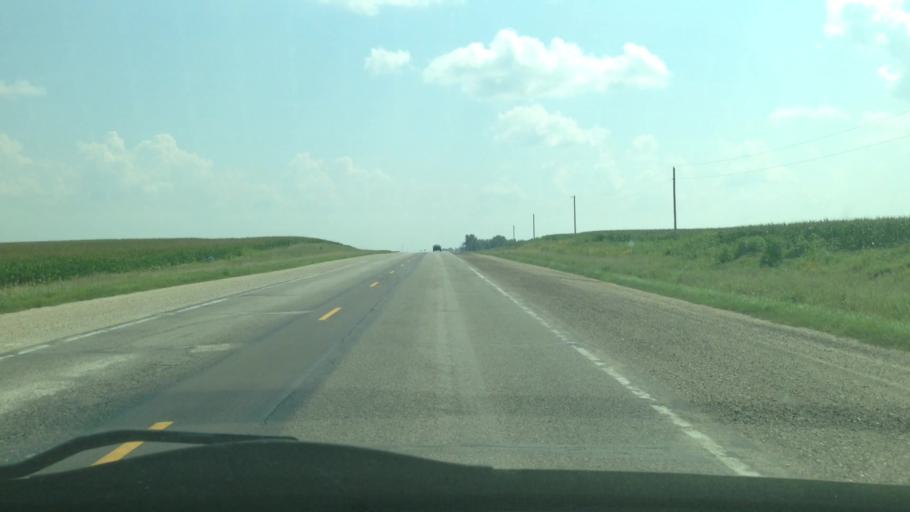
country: US
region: Iowa
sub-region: Howard County
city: Cresco
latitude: 43.3627
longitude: -92.2985
